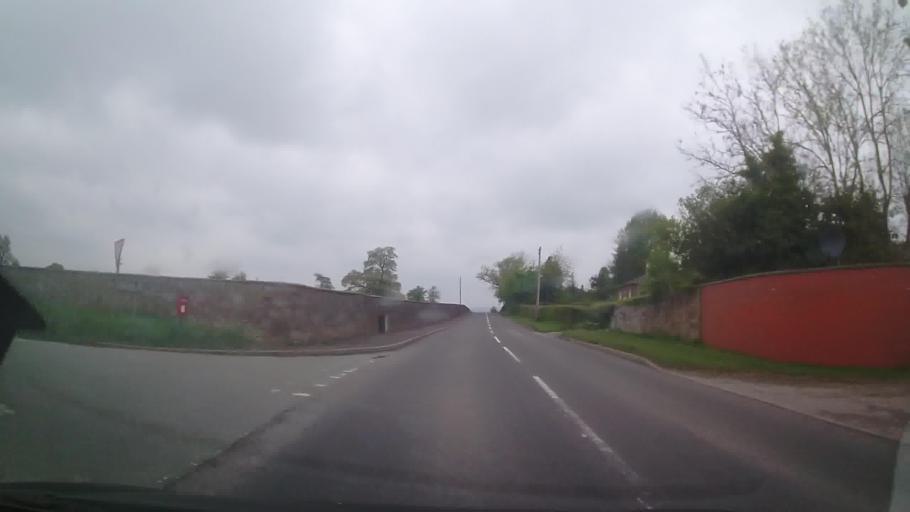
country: GB
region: Wales
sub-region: Wrexham
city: Ruabon
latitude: 52.9817
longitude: -3.0196
